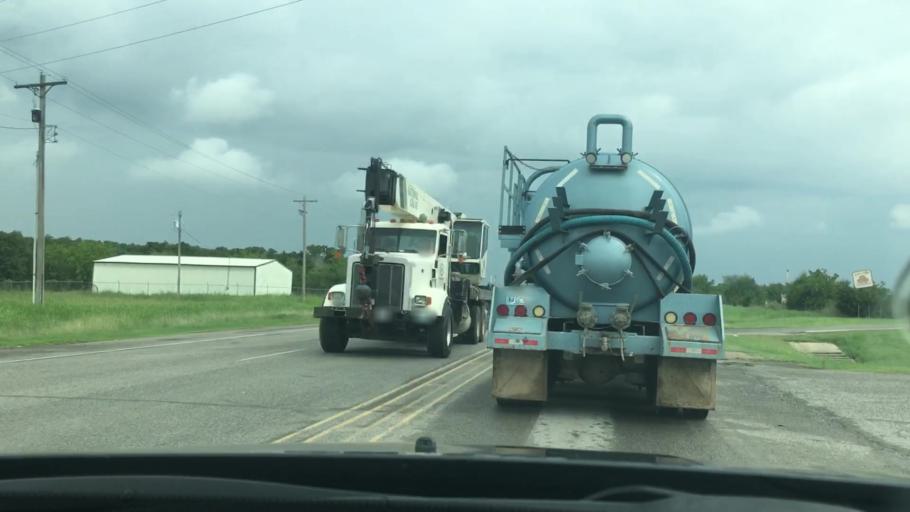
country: US
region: Oklahoma
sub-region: Carter County
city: Wilson
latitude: 34.1739
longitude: -97.4748
